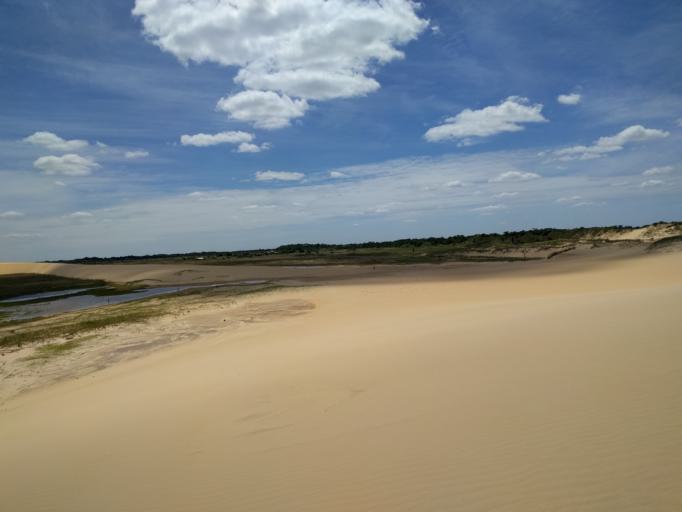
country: BO
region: Santa Cruz
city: Santa Cruz de la Sierra
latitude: -17.9453
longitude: -63.1527
